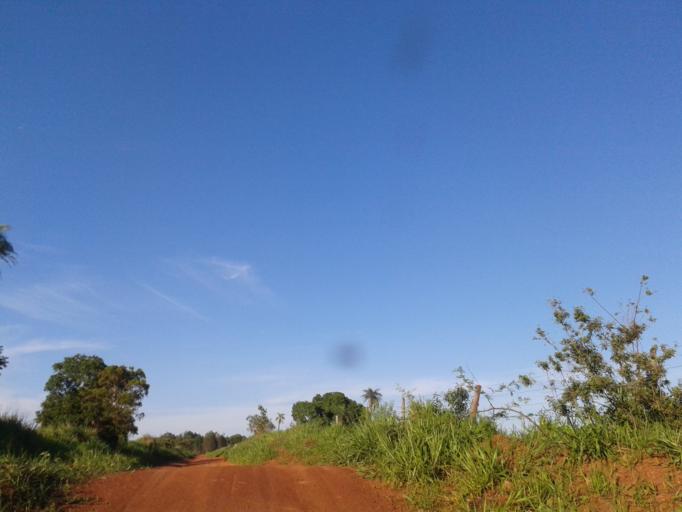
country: BR
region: Minas Gerais
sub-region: Santa Vitoria
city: Santa Vitoria
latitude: -18.9660
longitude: -49.8764
